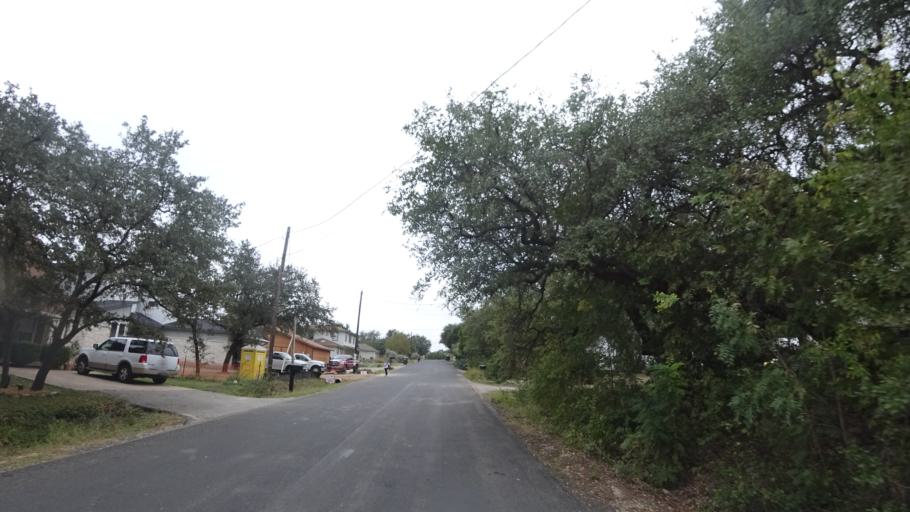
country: US
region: Texas
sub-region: Travis County
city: Hudson Bend
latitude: 30.3764
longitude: -97.9251
